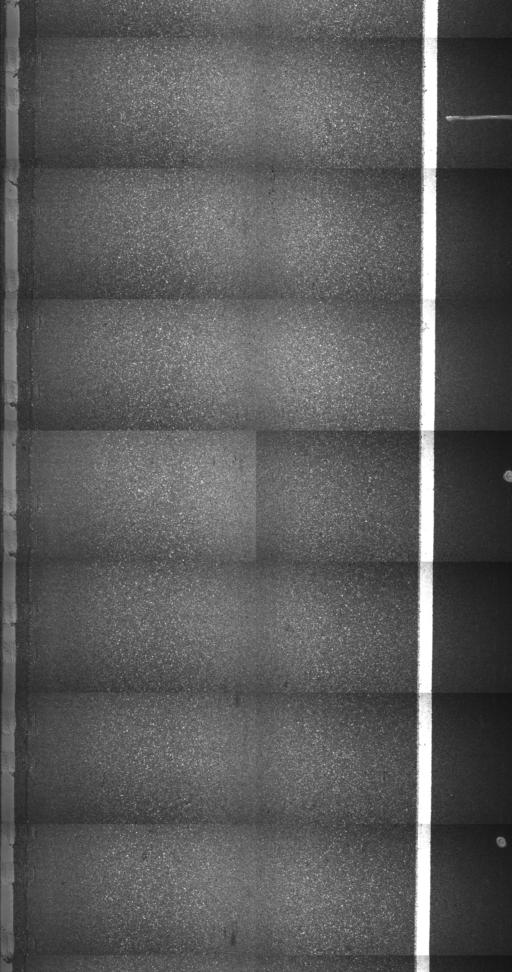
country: US
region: Vermont
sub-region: Orange County
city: Randolph
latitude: 43.7973
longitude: -72.6629
